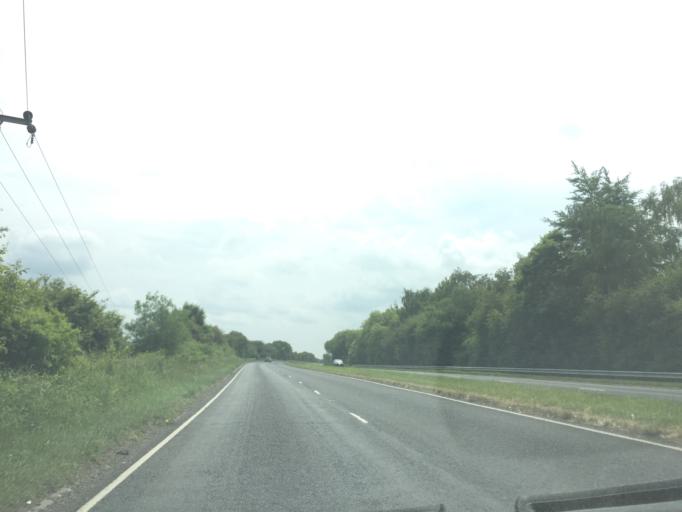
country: GB
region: England
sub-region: Hampshire
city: Alton
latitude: 51.1460
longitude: -0.9593
